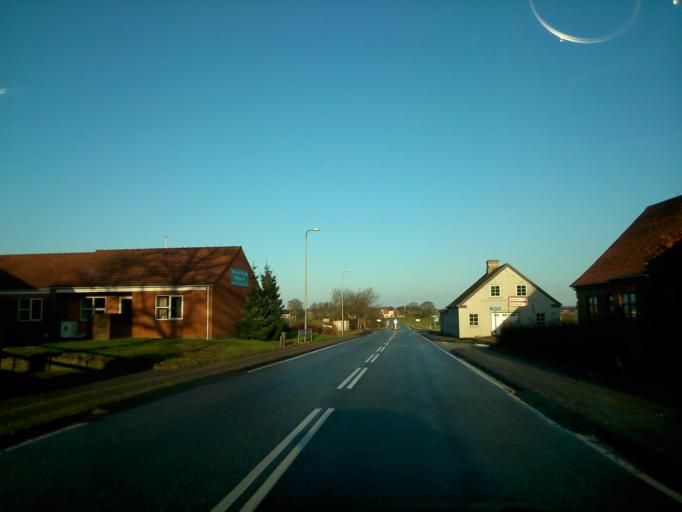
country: DK
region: Central Jutland
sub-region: Ringkobing-Skjern Kommune
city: Tarm
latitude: 55.9865
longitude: 8.5935
